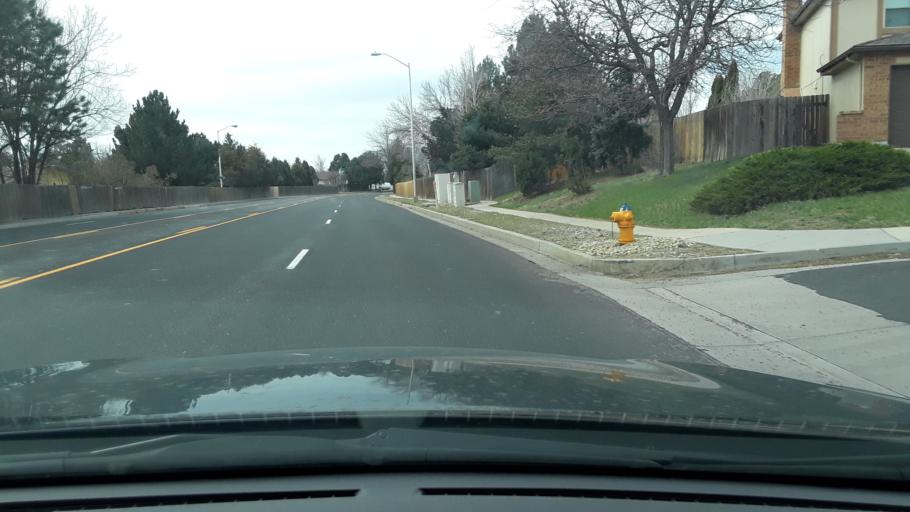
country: US
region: Colorado
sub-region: El Paso County
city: Air Force Academy
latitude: 38.9278
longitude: -104.8374
